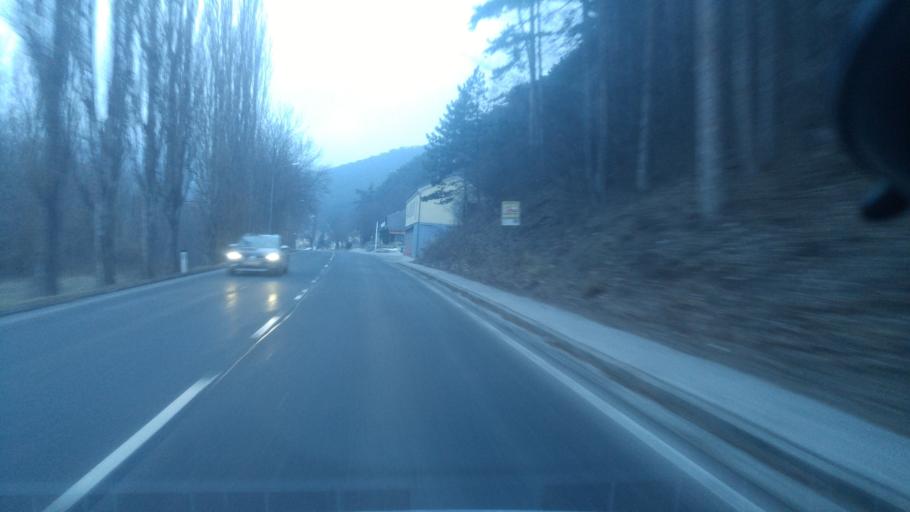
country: AT
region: Lower Austria
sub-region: Politischer Bezirk Baden
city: Weissenbach an der Triesting
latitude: 47.9776
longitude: 16.0692
